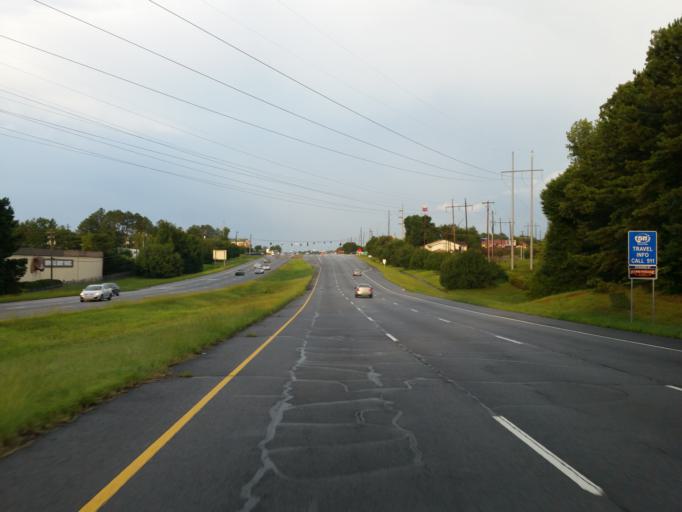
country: US
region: Georgia
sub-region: Cobb County
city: Smyrna
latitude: 33.9227
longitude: -84.4965
